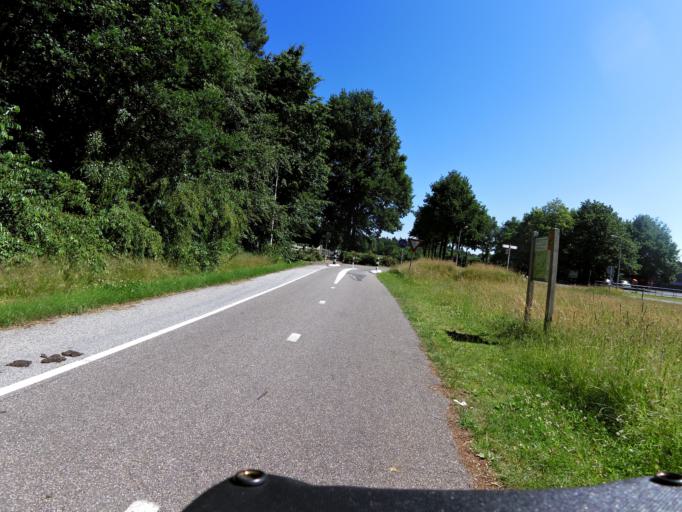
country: NL
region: Overijssel
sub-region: Gemeente Twenterand
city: Den Ham
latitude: 52.5422
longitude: 6.4811
